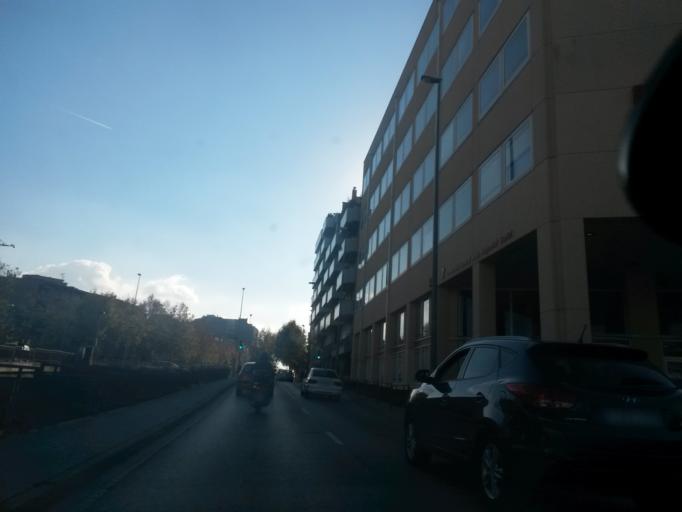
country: ES
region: Catalonia
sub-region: Provincia de Girona
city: Girona
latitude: 41.9798
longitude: 2.8110
